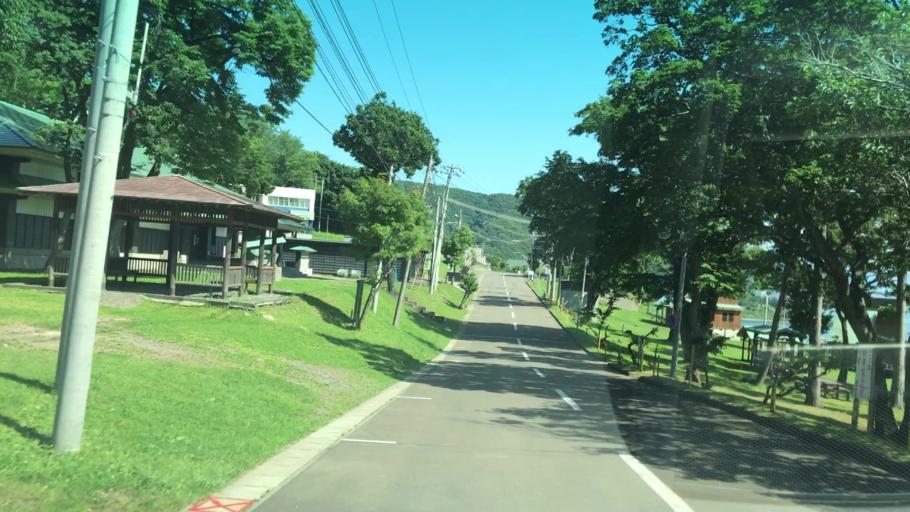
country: JP
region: Hokkaido
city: Iwanai
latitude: 43.1486
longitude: 140.4197
